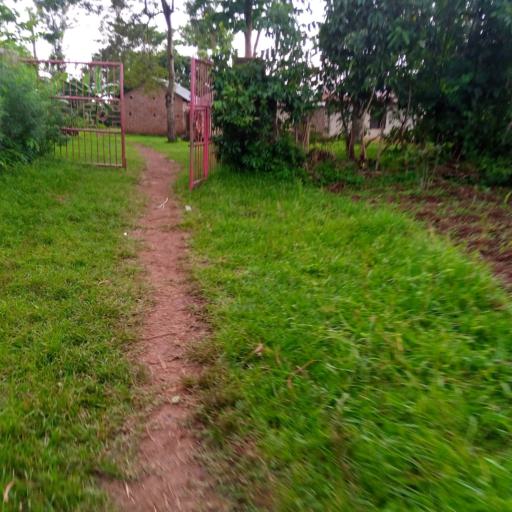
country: UG
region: Eastern Region
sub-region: Mbale District
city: Mbale
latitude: 1.1514
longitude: 34.1999
